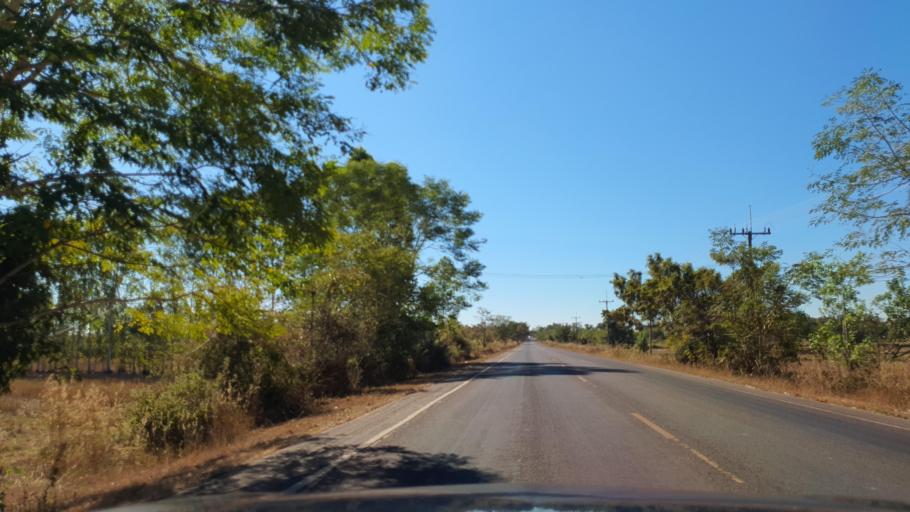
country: TH
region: Nakhon Phanom
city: Si Songkhram
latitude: 17.7442
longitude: 104.2861
